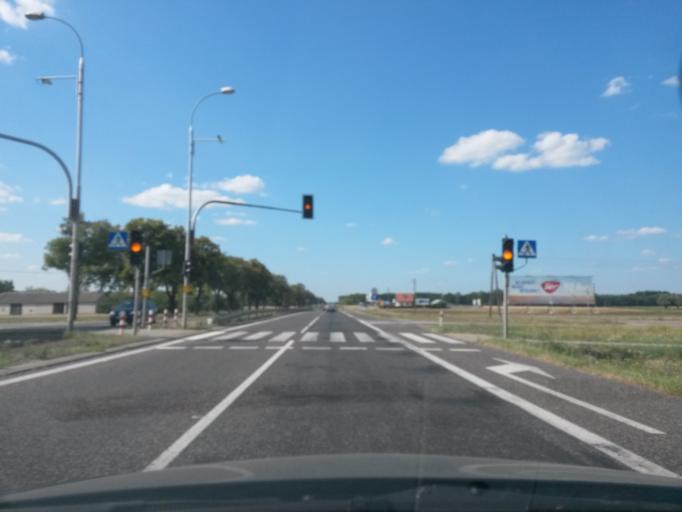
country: PL
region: Masovian Voivodeship
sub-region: Powiat plonski
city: Zaluski
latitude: 52.5305
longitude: 20.5200
